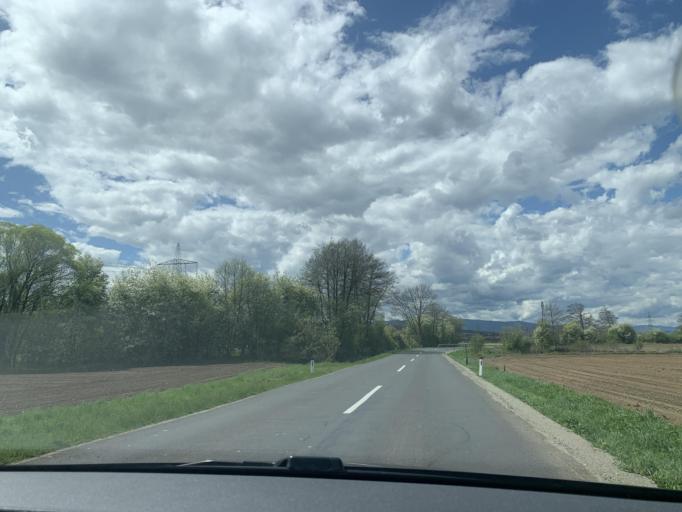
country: AT
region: Styria
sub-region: Politischer Bezirk Graz-Umgebung
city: Wundschuh
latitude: 46.9019
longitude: 15.4329
